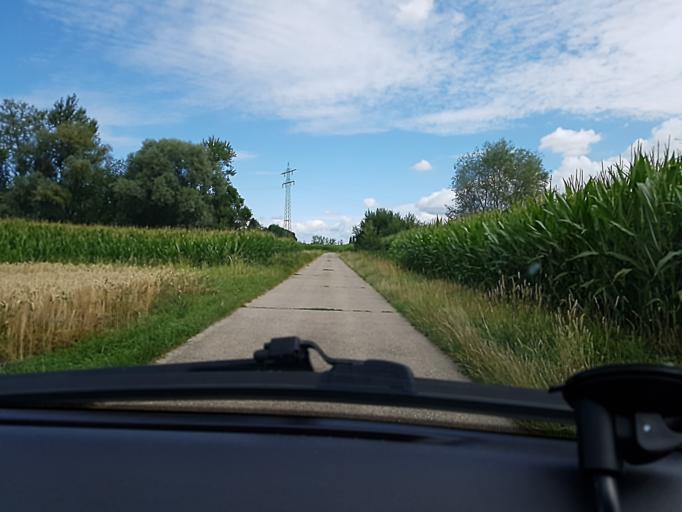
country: DE
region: Baden-Wuerttemberg
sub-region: Freiburg Region
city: Kehl
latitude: 48.5780
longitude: 7.8579
